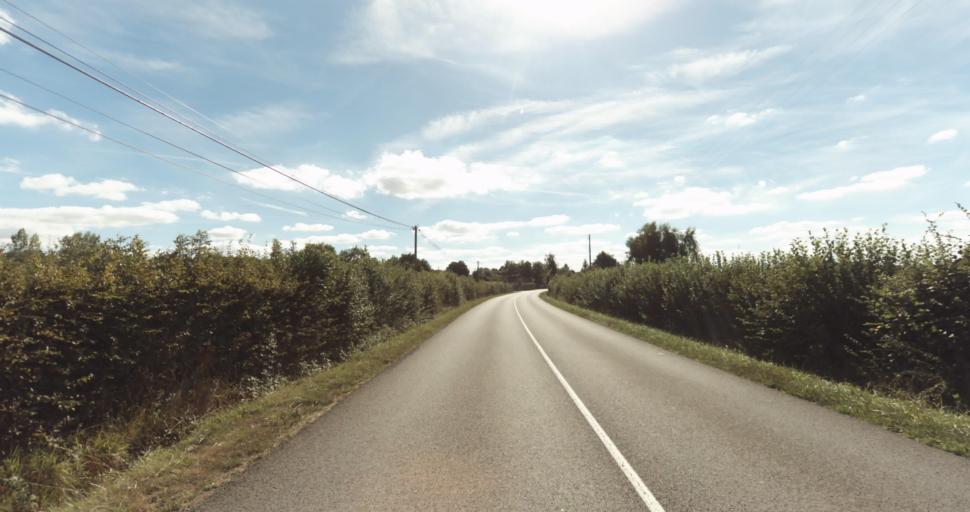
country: FR
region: Lower Normandy
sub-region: Departement de l'Orne
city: Vimoutiers
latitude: 48.9128
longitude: 0.1481
